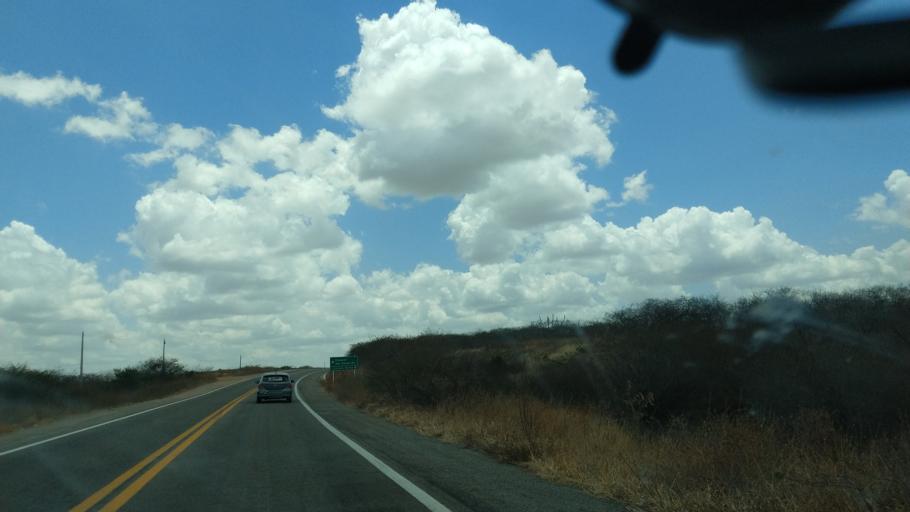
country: BR
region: Rio Grande do Norte
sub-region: Cerro Cora
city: Cerro Cora
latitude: -6.2063
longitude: -36.2815
